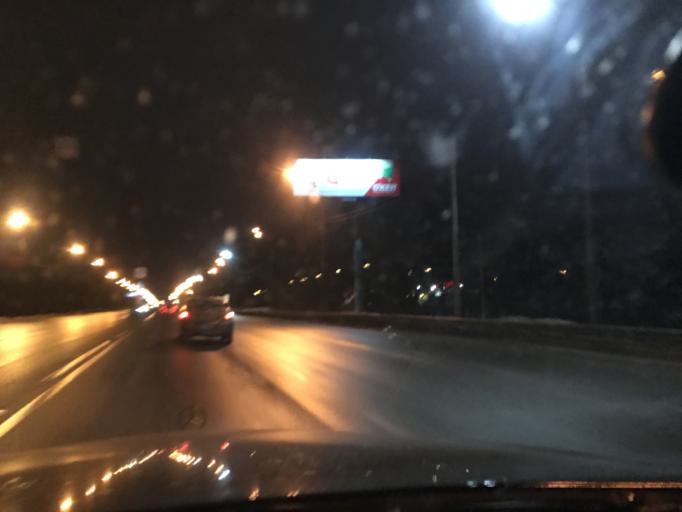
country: RU
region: Moskovskaya
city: Noginsk
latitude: 55.8342
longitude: 38.3882
